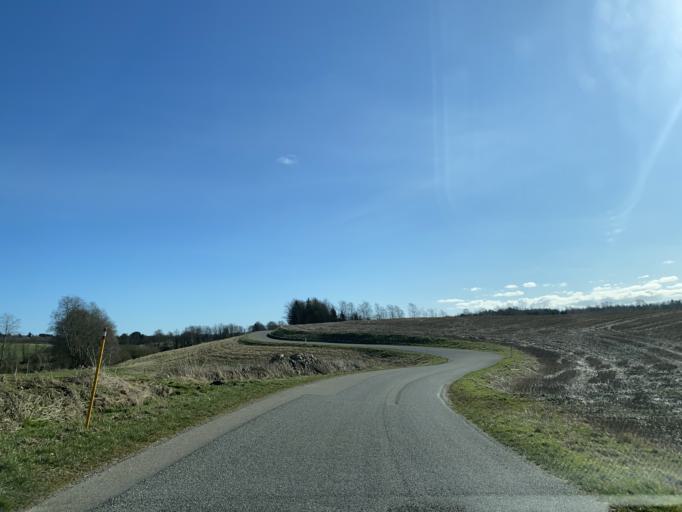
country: DK
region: Central Jutland
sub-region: Arhus Kommune
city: Framlev
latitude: 56.1820
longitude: 10.0227
